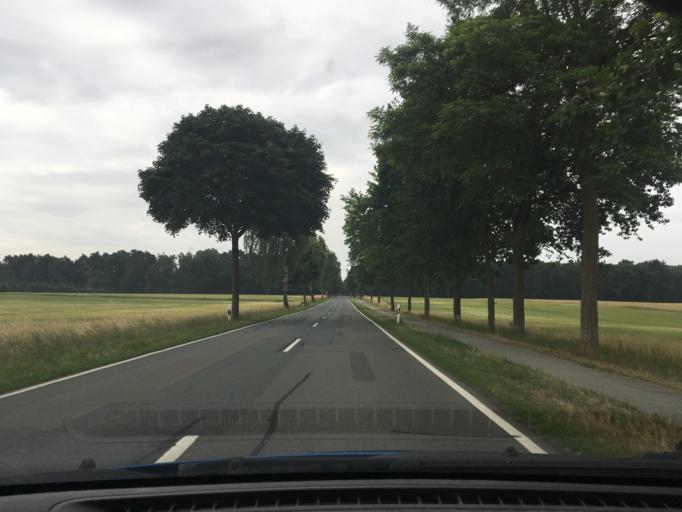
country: DE
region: Lower Saxony
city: Wenzendorf
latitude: 53.3422
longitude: 9.7557
